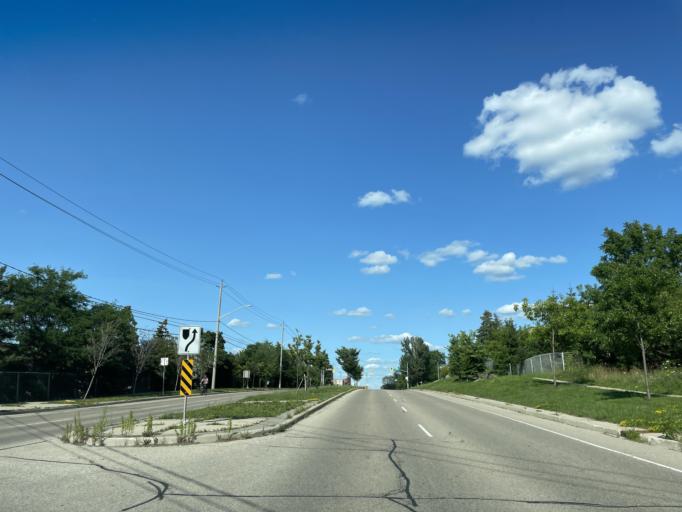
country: CA
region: Ontario
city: Kitchener
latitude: 43.4324
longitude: -80.5235
